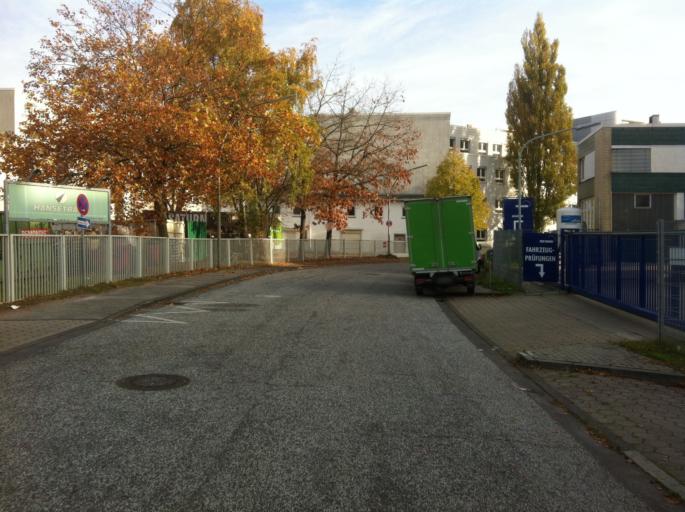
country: DE
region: Hamburg
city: Altona
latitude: 53.5718
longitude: 9.9392
